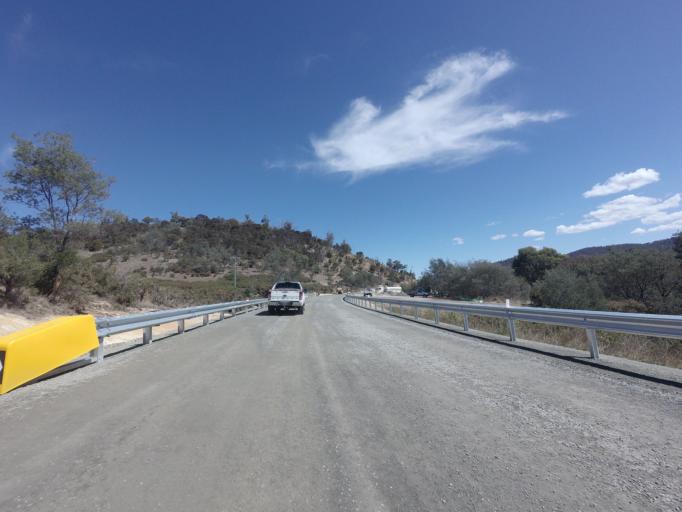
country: AU
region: Tasmania
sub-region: Break O'Day
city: St Helens
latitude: -41.6557
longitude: 147.9222
